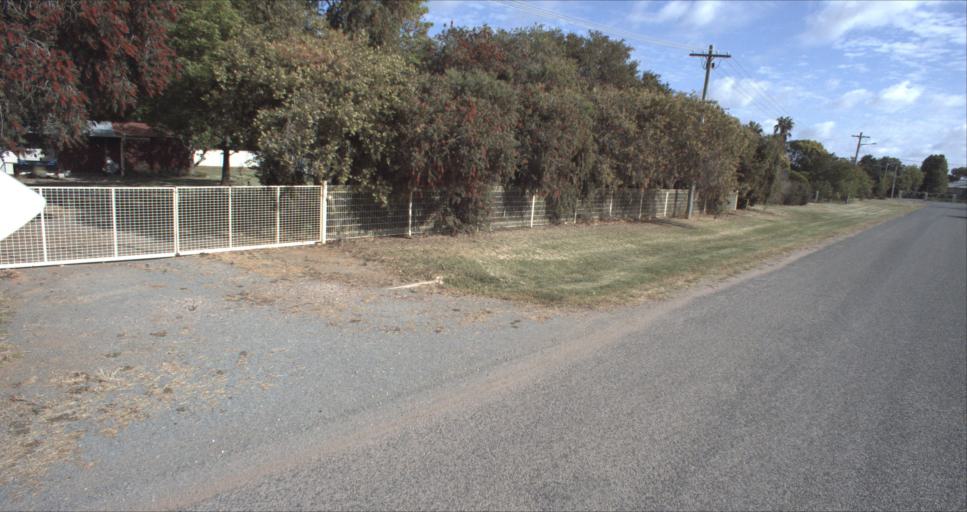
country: AU
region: New South Wales
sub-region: Leeton
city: Leeton
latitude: -34.5694
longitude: 146.3919
